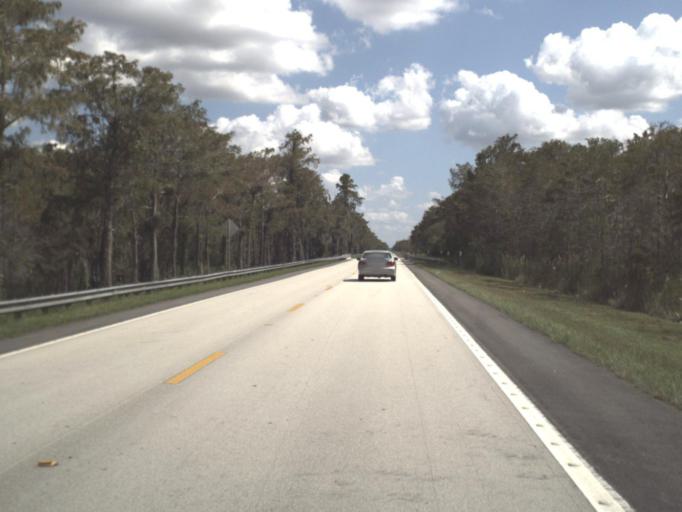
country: US
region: Florida
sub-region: Miami-Dade County
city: Kendall West
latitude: 25.8407
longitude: -80.9142
